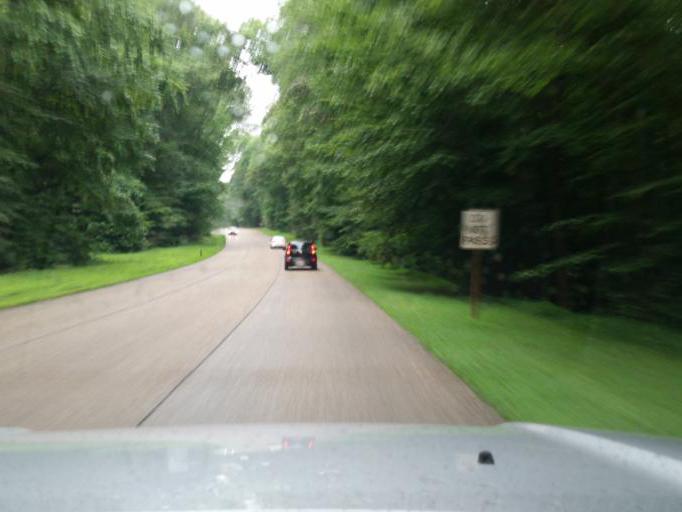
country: US
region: Virginia
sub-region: City of Williamsburg
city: Williamsburg
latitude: 37.2787
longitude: -76.6691
